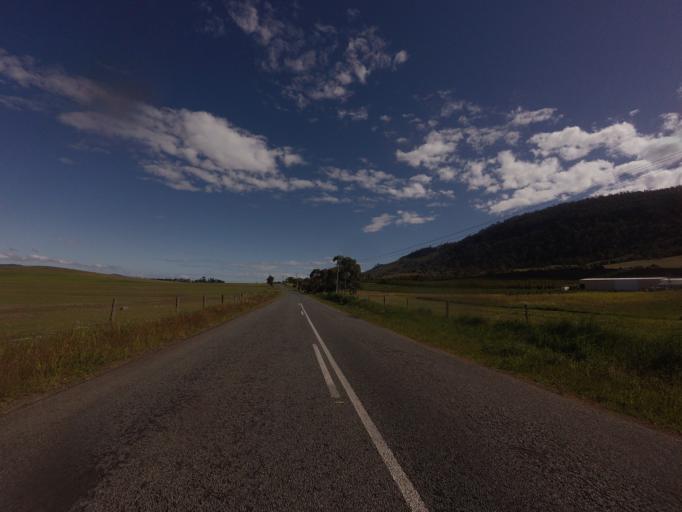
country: AU
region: Tasmania
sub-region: Sorell
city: Sorell
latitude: -42.6259
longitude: 147.4287
